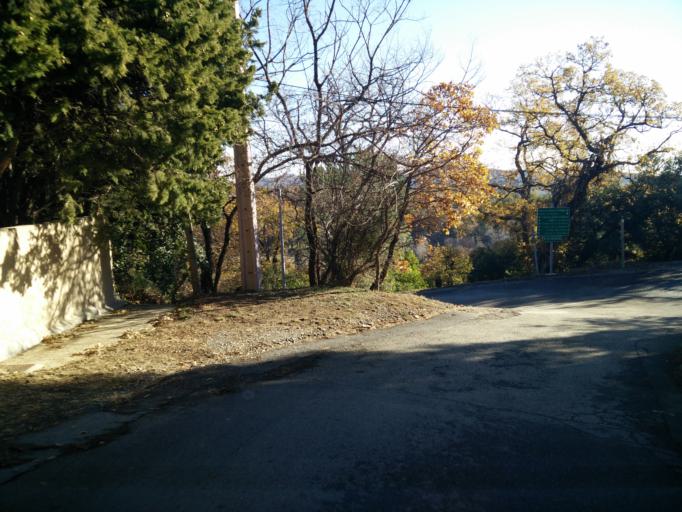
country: FR
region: Provence-Alpes-Cote d'Azur
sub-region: Departement du Var
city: La Garde-Freinet
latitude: 43.3102
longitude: 6.4786
